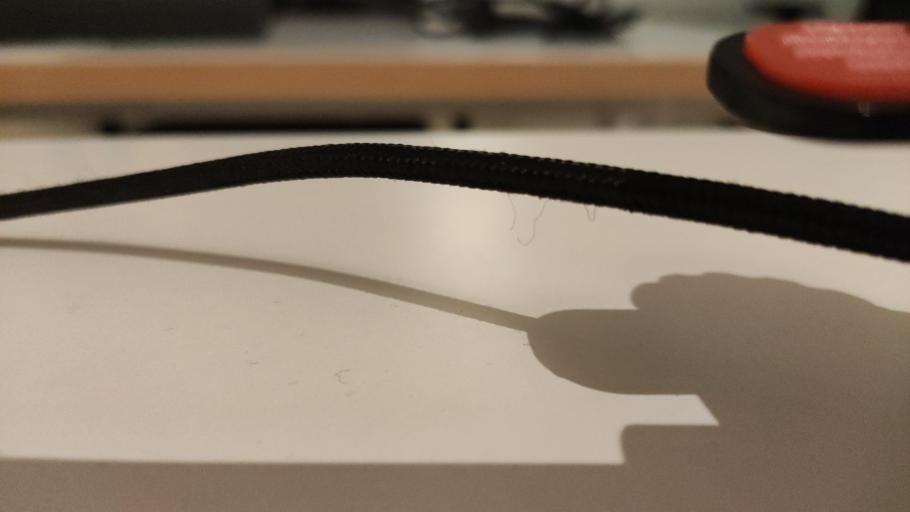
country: RU
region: Moskovskaya
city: Lopatinskiy
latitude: 55.3806
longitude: 38.7572
